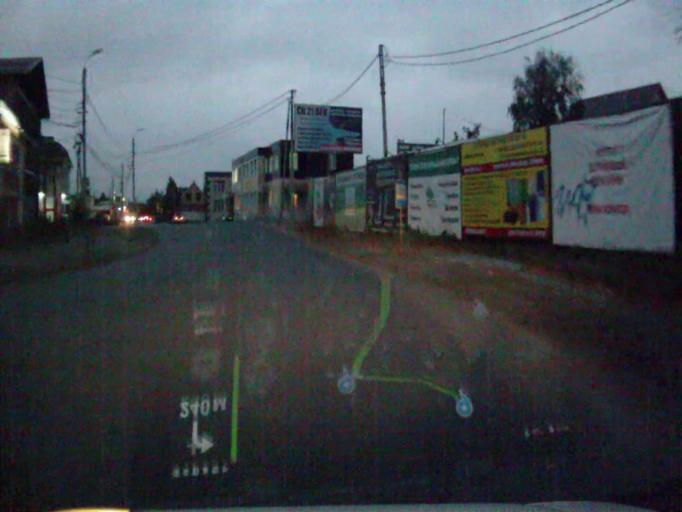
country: RU
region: Chelyabinsk
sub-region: Gorod Chelyabinsk
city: Chelyabinsk
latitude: 55.1561
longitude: 61.2998
